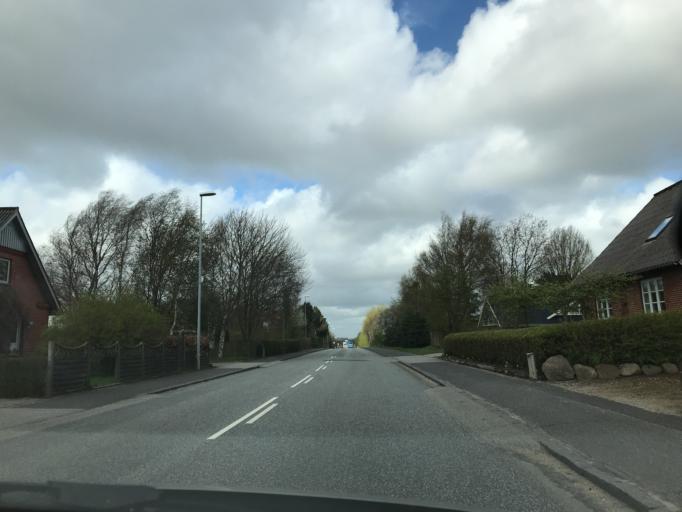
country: DK
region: Central Jutland
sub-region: Viborg Kommune
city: Stoholm
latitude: 56.3907
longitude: 8.9958
